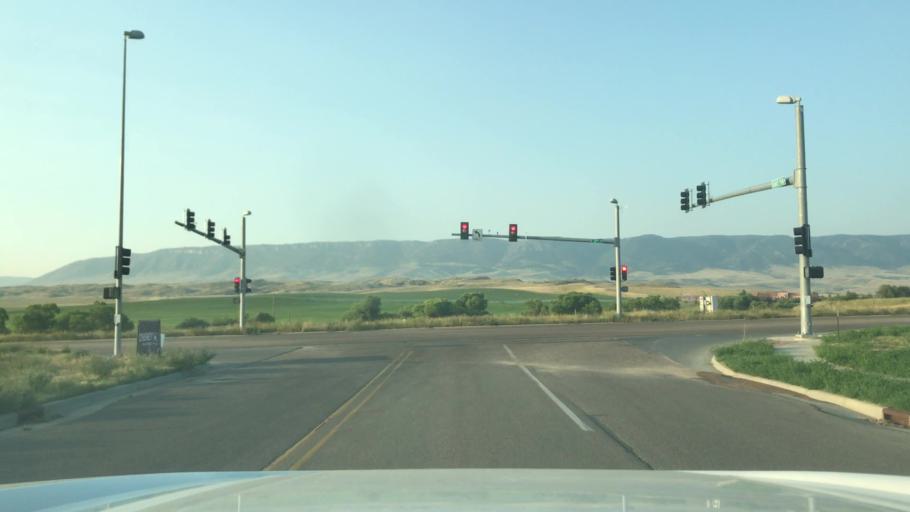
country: US
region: Wyoming
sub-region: Natrona County
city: Evansville
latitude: 42.8400
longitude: -106.2238
